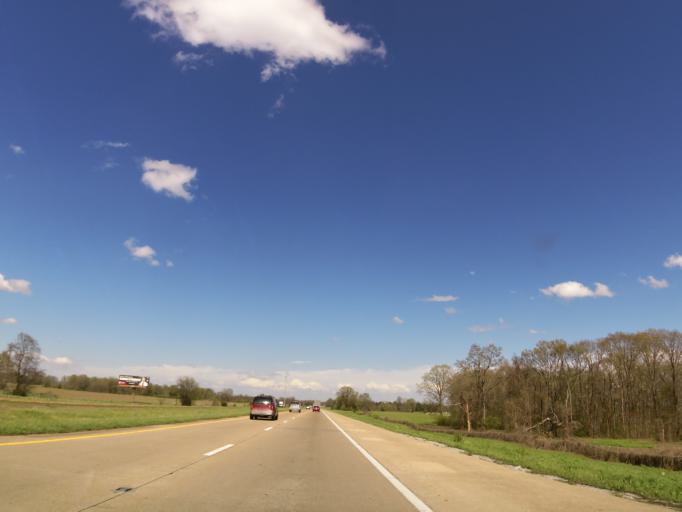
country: US
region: Tennessee
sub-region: Gibson County
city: Medina
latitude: 35.7005
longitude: -88.6857
